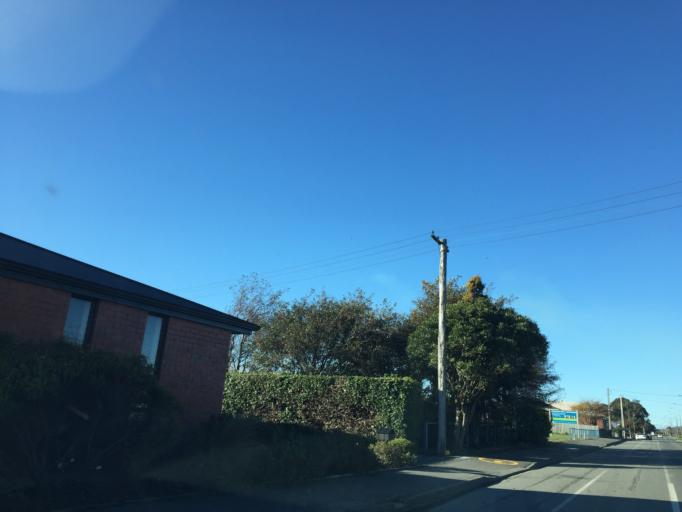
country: NZ
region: Southland
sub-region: Invercargill City
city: Invercargill
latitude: -46.3755
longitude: 168.3485
